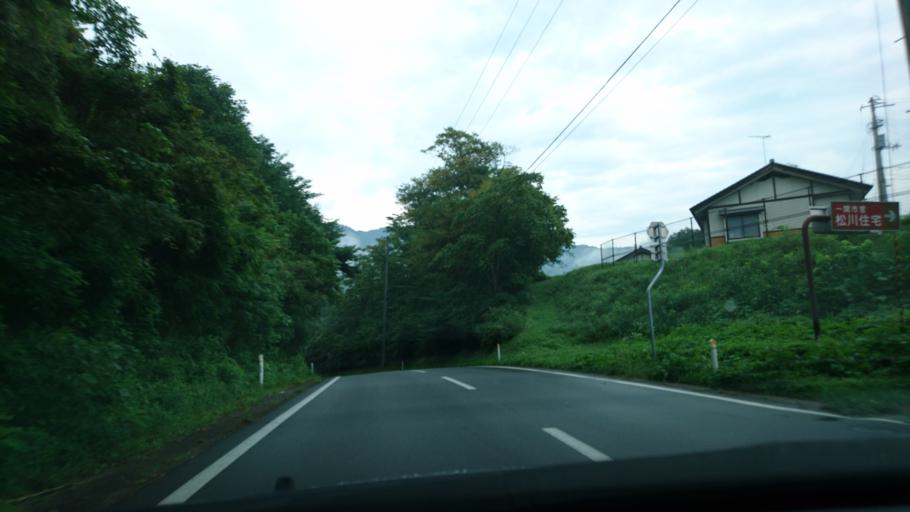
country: JP
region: Iwate
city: Ichinoseki
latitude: 38.9520
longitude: 141.2529
